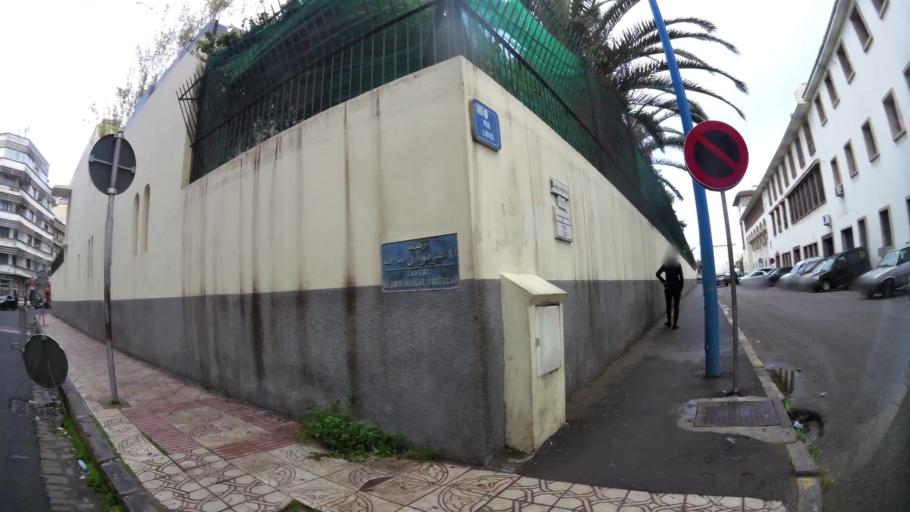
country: MA
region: Grand Casablanca
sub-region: Casablanca
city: Casablanca
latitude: 33.5901
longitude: -7.6171
